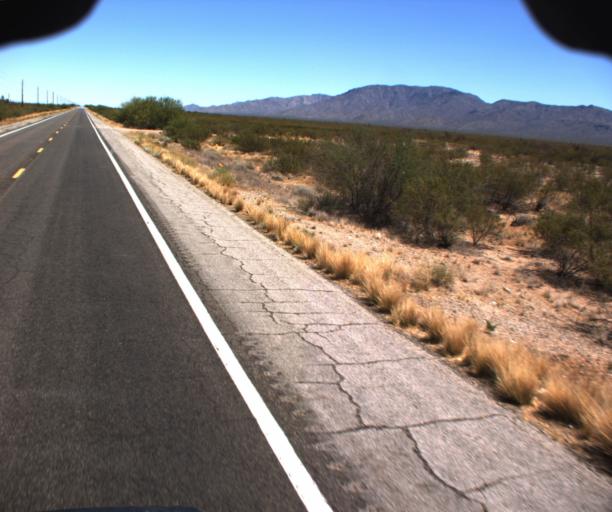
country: US
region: Arizona
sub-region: La Paz County
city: Salome
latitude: 33.8334
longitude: -113.4994
